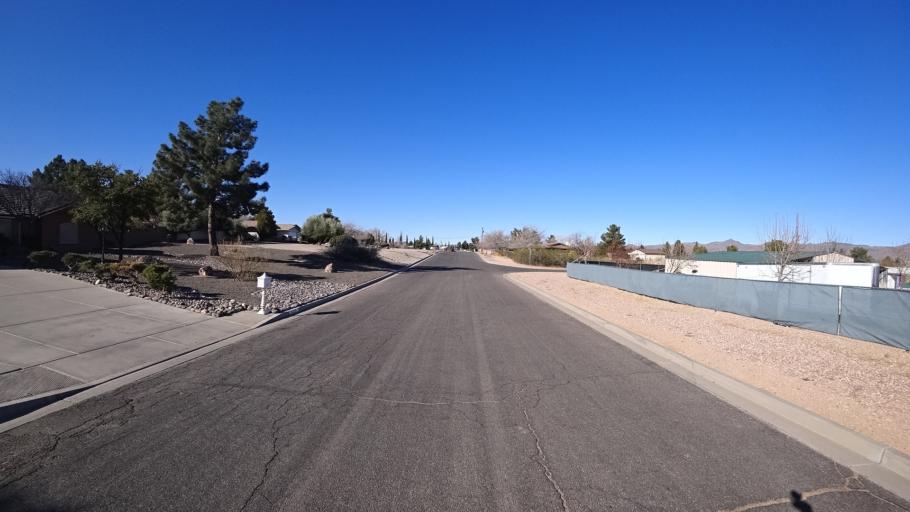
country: US
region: Arizona
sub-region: Mohave County
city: Kingman
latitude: 35.1994
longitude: -114.0042
